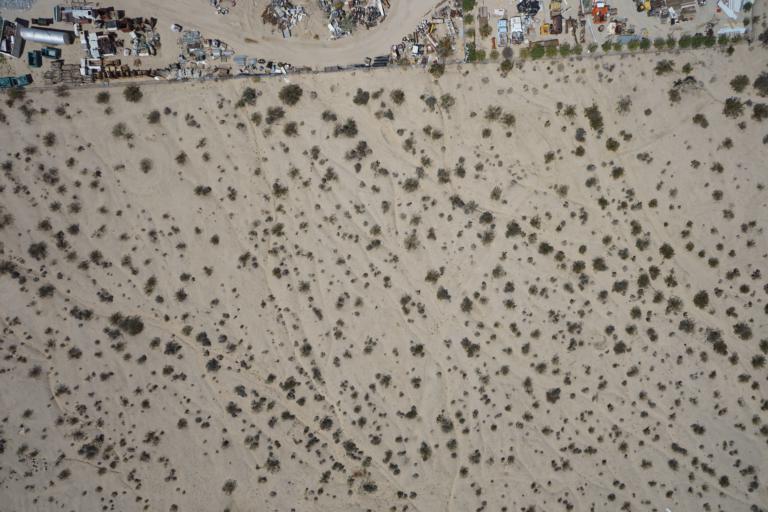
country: US
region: California
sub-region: San Bernardino County
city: Twentynine Palms
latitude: 34.1304
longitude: -116.0600
